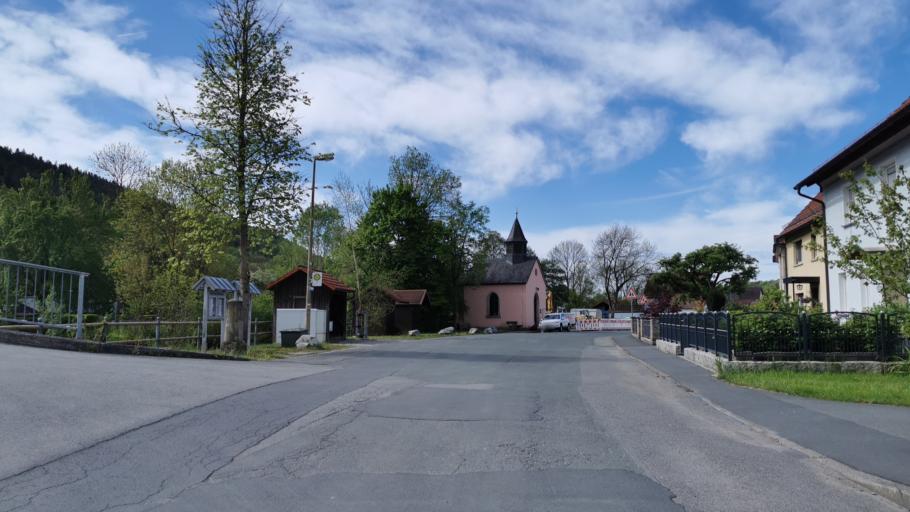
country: DE
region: Bavaria
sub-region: Upper Franconia
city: Kronach
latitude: 50.2592
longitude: 11.3478
